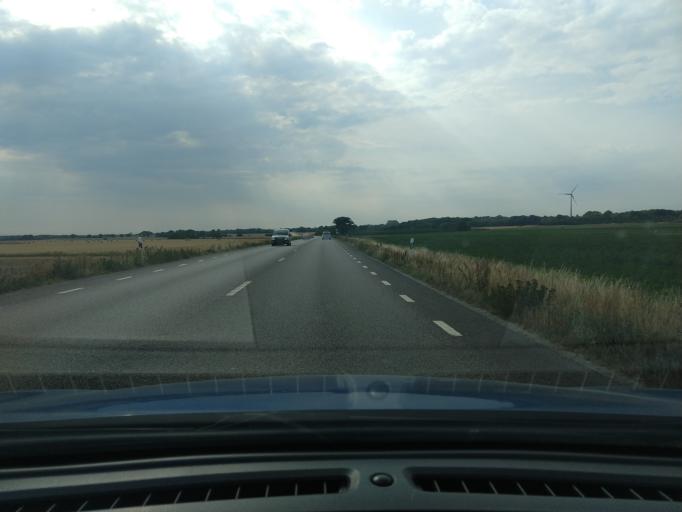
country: SE
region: Blekinge
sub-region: Karlskrona Kommun
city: Jaemjoe
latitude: 56.1839
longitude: 15.7518
